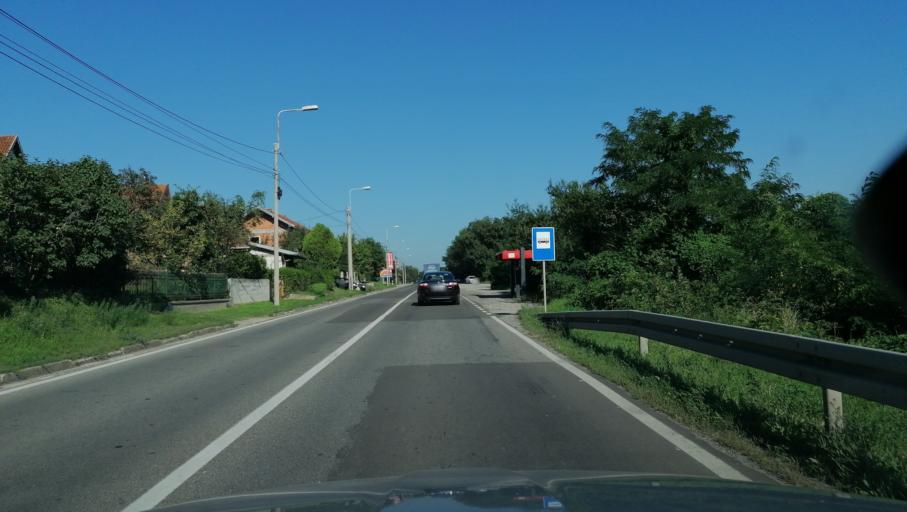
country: RS
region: Central Serbia
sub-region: Raski Okrug
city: Kraljevo
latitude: 43.7204
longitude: 20.6364
